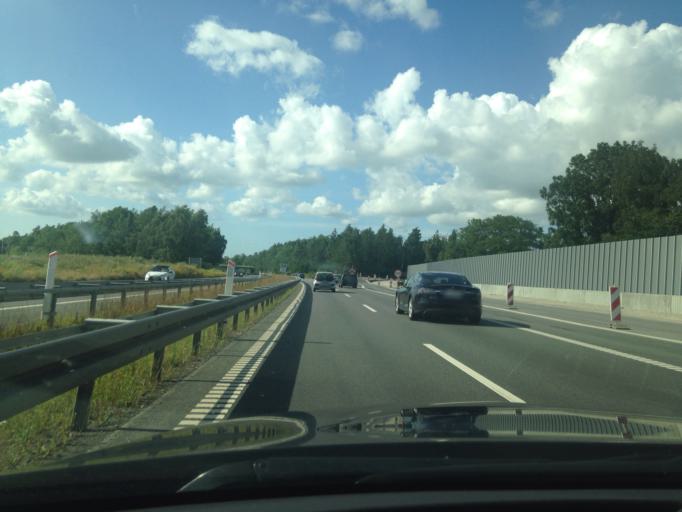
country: DK
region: Capital Region
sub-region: Horsholm Kommune
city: Horsholm
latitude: 55.8564
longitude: 12.4970
